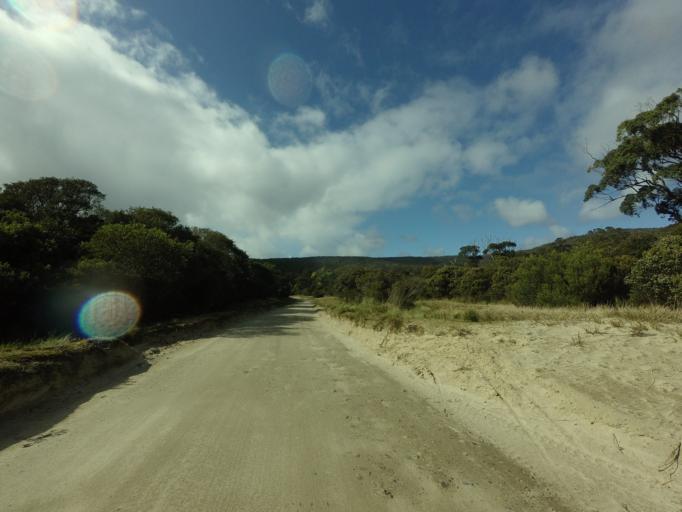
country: AU
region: Tasmania
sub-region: Huon Valley
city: Geeveston
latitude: -43.5814
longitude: 146.8898
